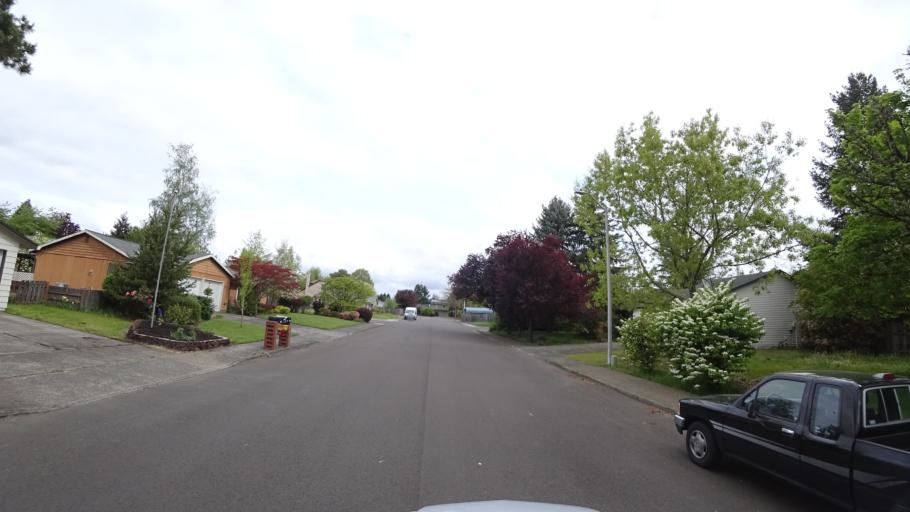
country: US
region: Oregon
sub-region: Washington County
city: Hillsboro
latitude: 45.5338
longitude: -122.9757
